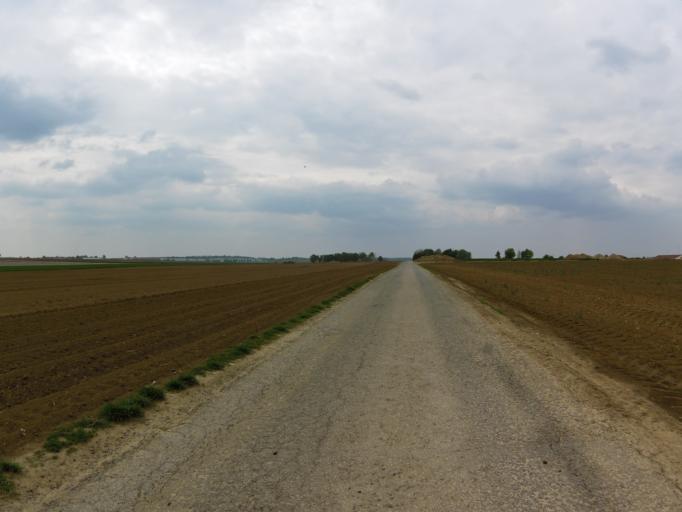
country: DE
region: Bavaria
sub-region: Regierungsbezirk Unterfranken
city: Unterpleichfeld
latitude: 49.8622
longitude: 10.0455
